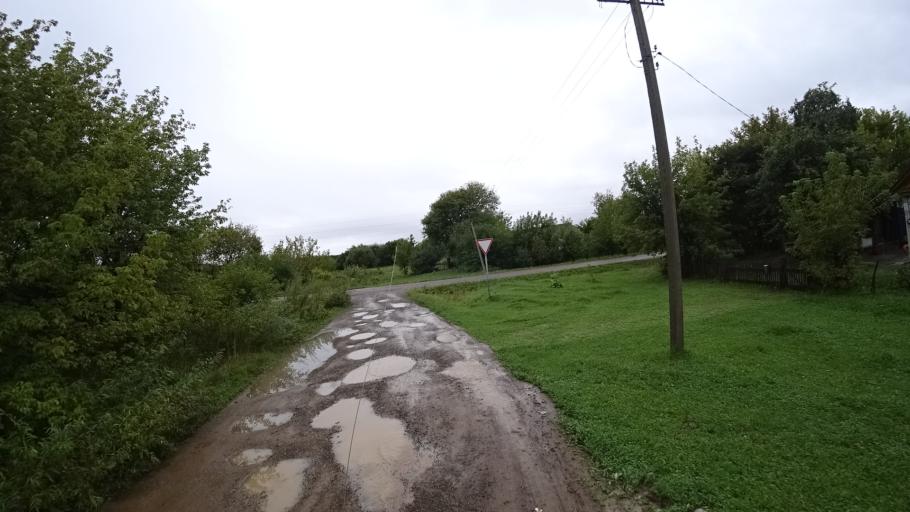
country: RU
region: Primorskiy
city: Monastyrishche
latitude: 44.2730
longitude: 132.4251
